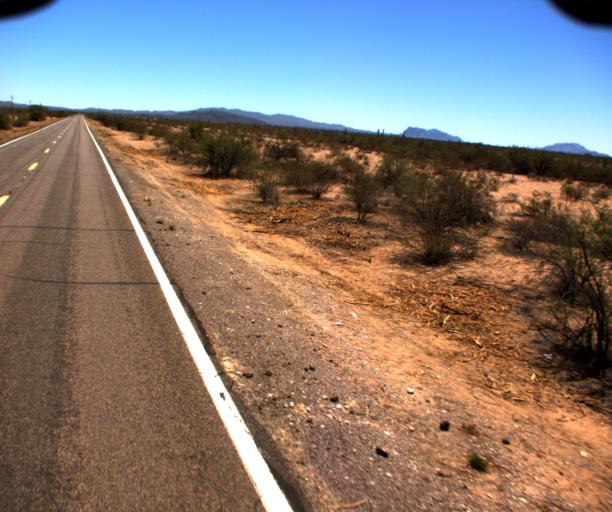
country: US
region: Arizona
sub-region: Pima County
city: Sells
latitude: 32.1821
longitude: -112.3397
